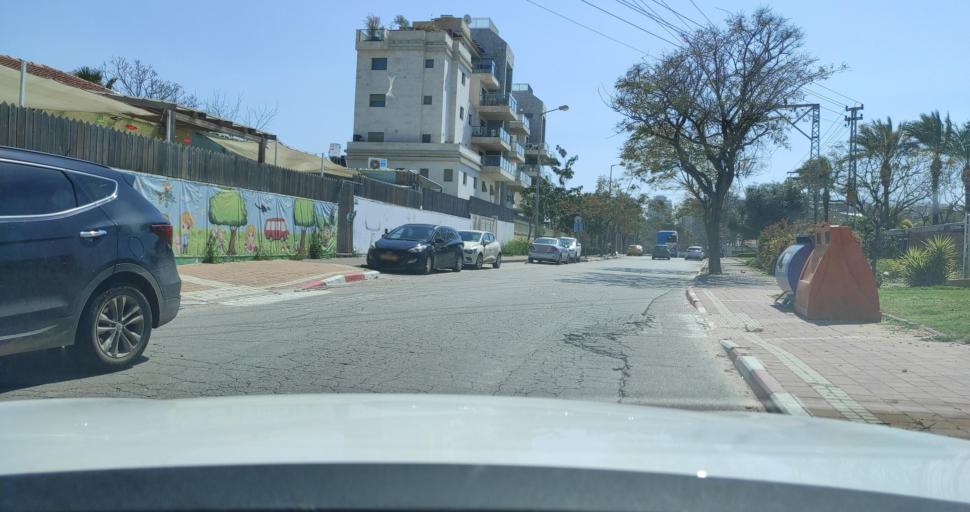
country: IL
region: Central District
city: Nordiyya
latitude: 32.3105
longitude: 34.8817
